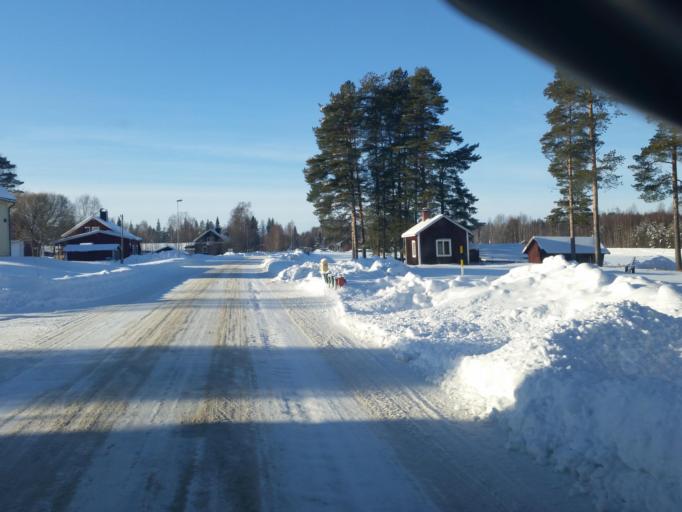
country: SE
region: Norrbotten
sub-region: Pitea Kommun
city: Bergsviken
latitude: 65.3132
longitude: 21.3426
